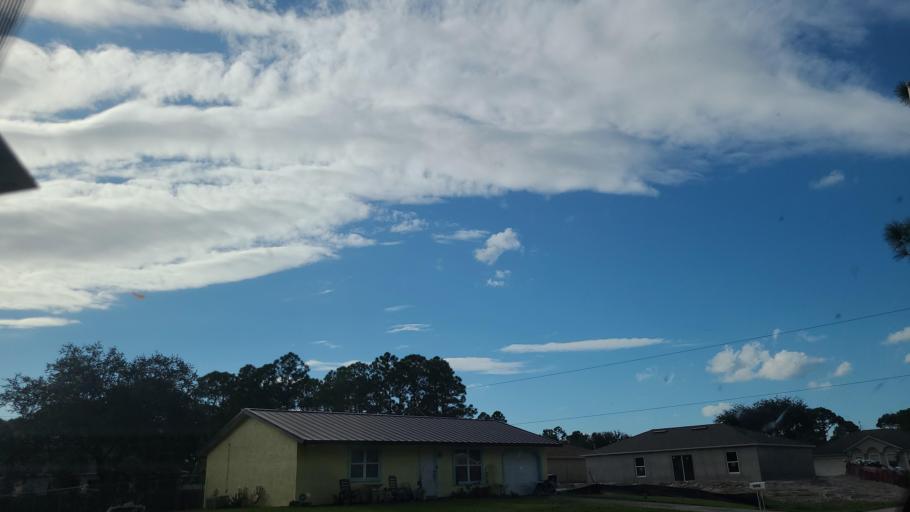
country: US
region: Florida
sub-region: Brevard County
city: Palm Bay
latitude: 27.9737
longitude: -80.6592
